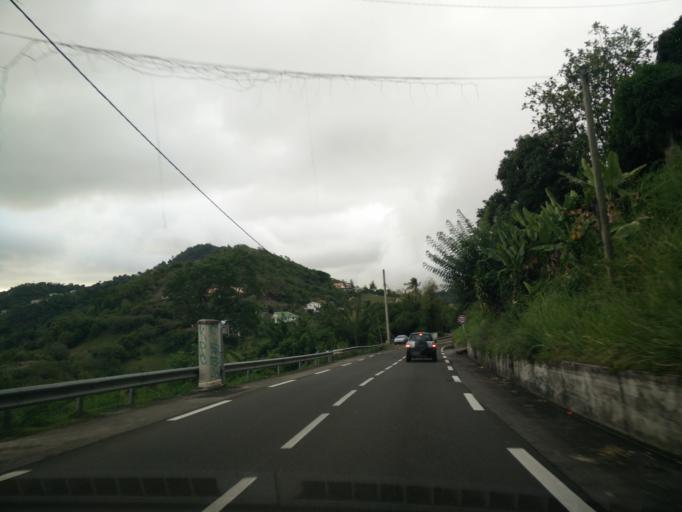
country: MQ
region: Martinique
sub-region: Martinique
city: Le Marin
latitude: 14.4898
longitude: -60.8603
